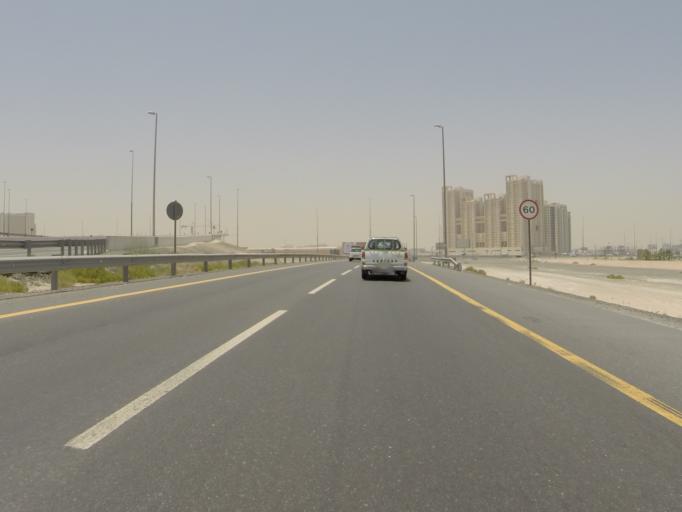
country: AE
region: Dubai
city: Dubai
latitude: 25.0450
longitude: 55.1973
